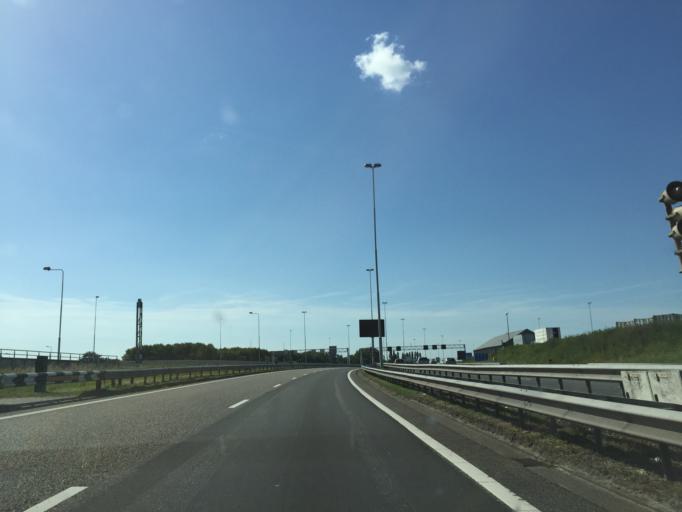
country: NL
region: South Holland
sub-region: Gemeente Schiedam
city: Schiedam
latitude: 51.8941
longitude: 4.3762
